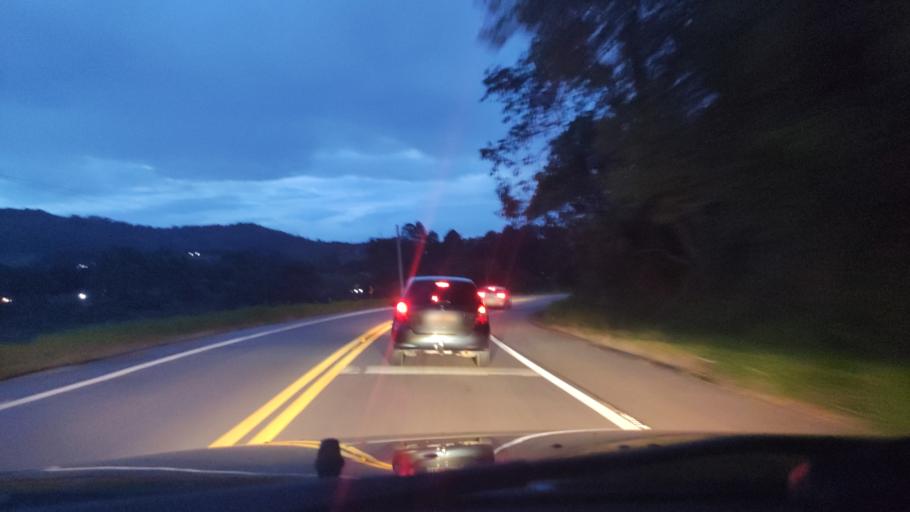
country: BR
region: Sao Paulo
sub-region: Socorro
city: Socorro
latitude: -22.5599
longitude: -46.5525
